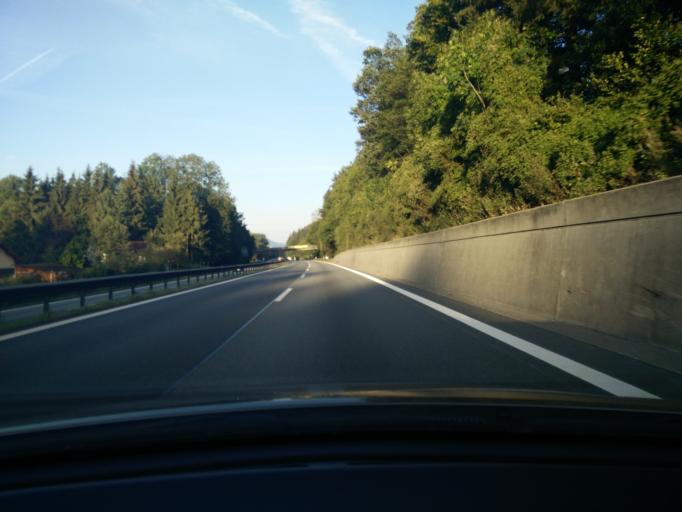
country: DE
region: Bavaria
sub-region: Upper Bavaria
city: Samerberg
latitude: 47.7981
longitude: 12.2307
